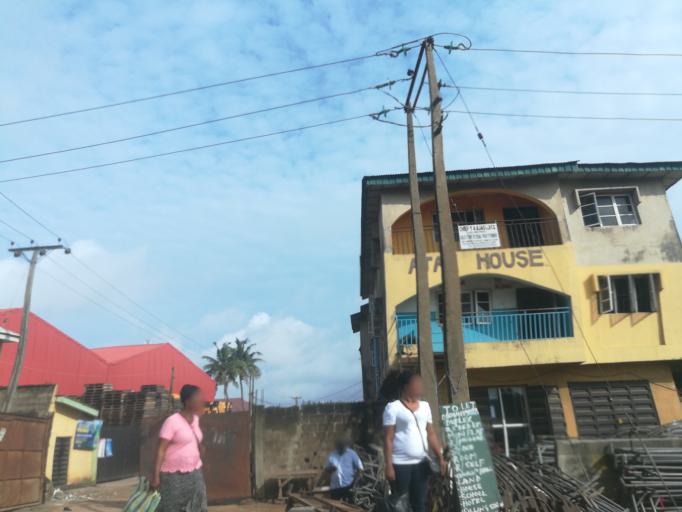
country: NG
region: Lagos
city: Agege
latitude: 6.6137
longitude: 3.3180
